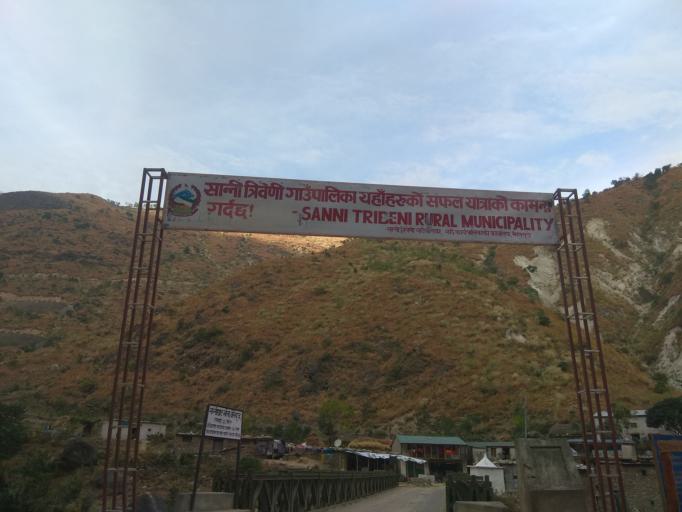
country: NP
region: Far Western
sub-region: Seti Zone
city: Achham
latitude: 29.2234
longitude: 81.6271
